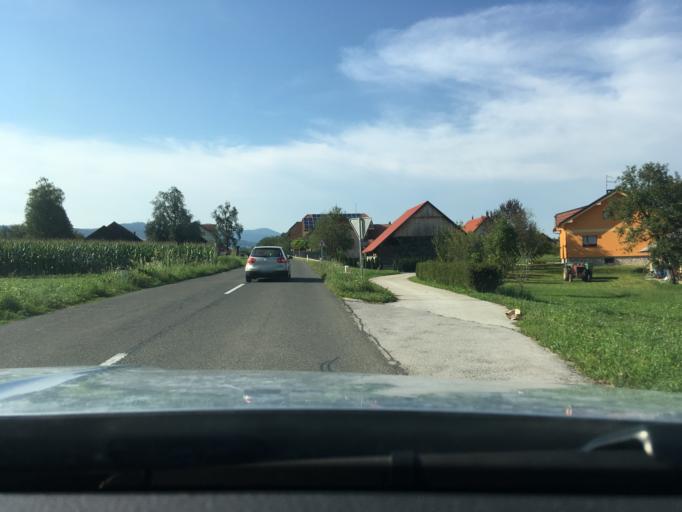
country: SI
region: Crnomelj
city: Crnomelj
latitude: 45.5400
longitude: 15.1606
